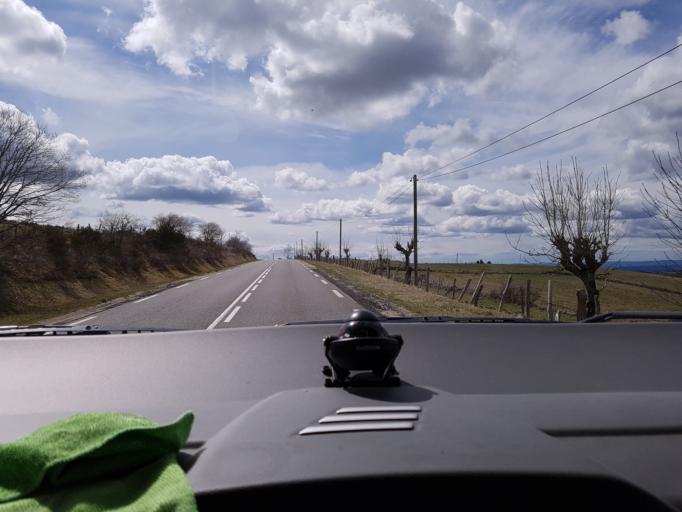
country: FR
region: Midi-Pyrenees
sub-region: Departement de l'Aveyron
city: Laguiole
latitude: 44.7167
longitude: 2.8654
